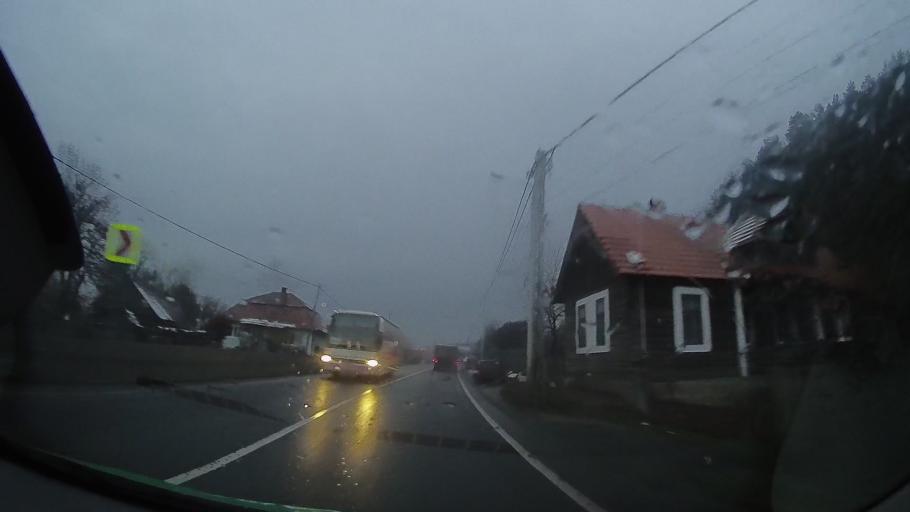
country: RO
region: Harghita
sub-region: Comuna Lazarea
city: Lazarea
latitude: 46.7507
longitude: 25.5202
